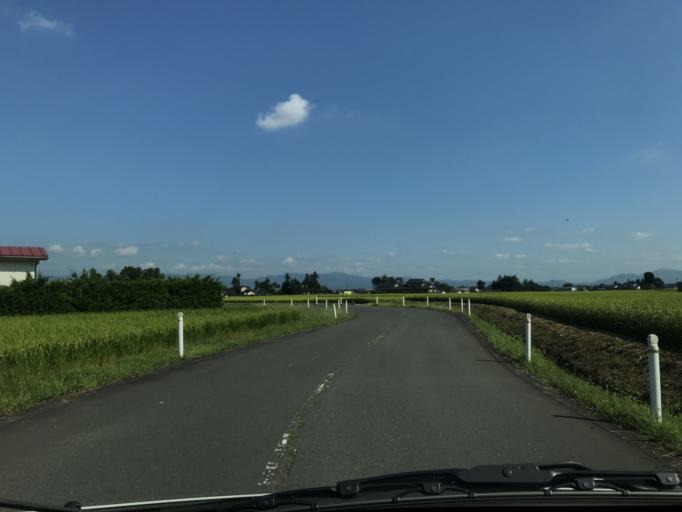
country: JP
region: Iwate
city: Mizusawa
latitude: 39.1588
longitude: 141.1028
